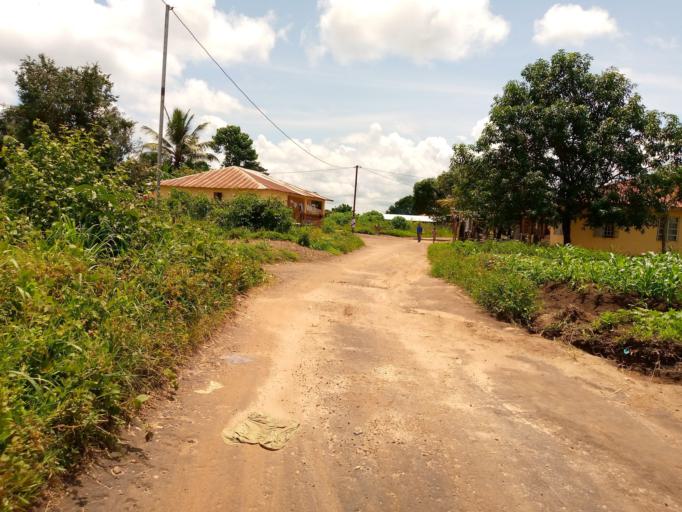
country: SL
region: Northern Province
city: Magburaka
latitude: 8.7177
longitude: -11.9609
